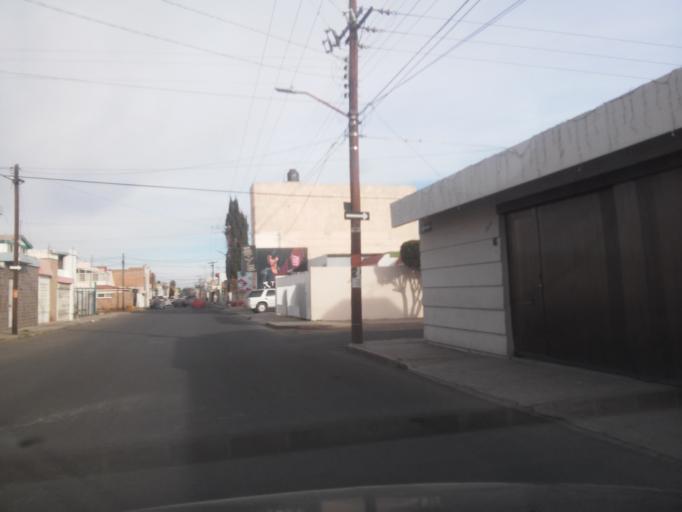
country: MX
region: Durango
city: Victoria de Durango
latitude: 24.0252
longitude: -104.6505
